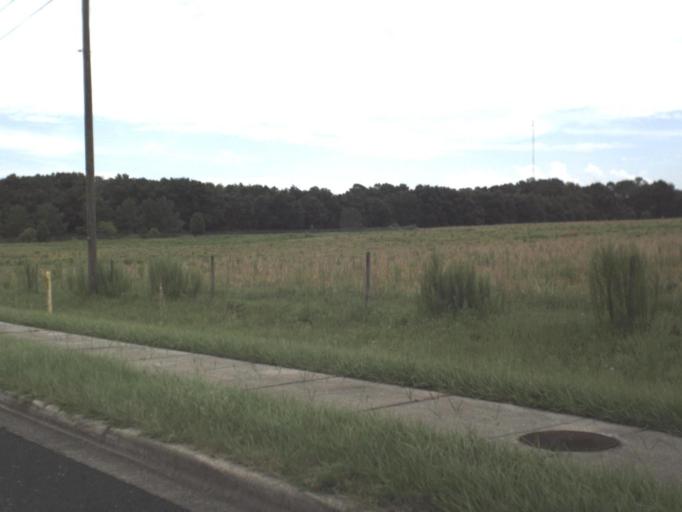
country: US
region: Florida
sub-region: Citrus County
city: Lecanto
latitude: 28.8517
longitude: -82.4932
